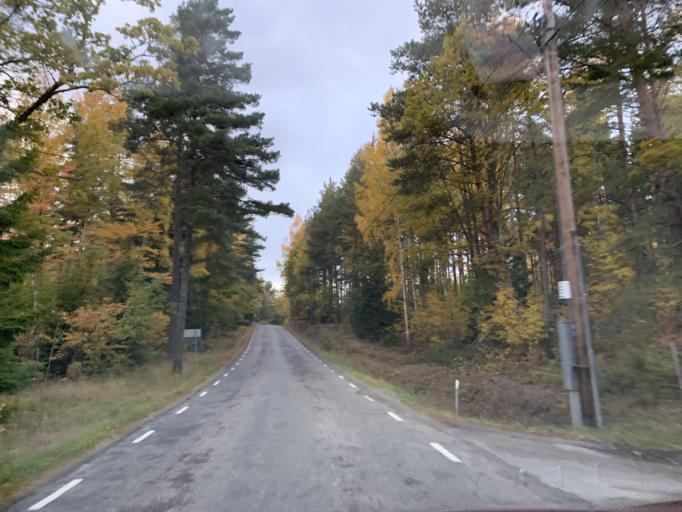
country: SE
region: Stockholm
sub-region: Nynashamns Kommun
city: Osmo
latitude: 58.9175
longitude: 17.7790
